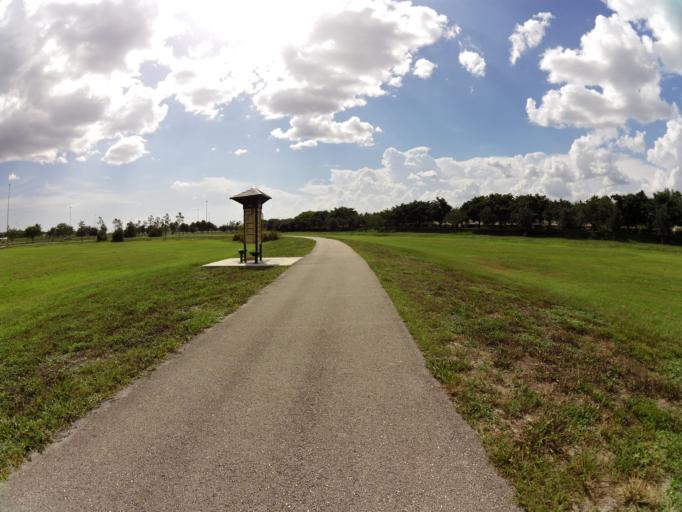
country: US
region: Florida
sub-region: Broward County
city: Southwest Ranches
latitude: 26.0652
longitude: -80.3486
